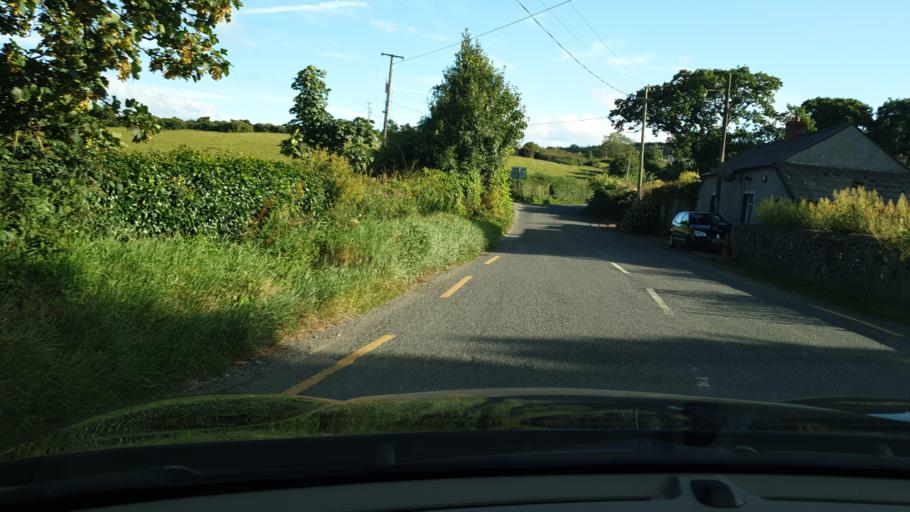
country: IE
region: Leinster
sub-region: An Mhi
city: Stamullin
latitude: 53.6163
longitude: -6.2938
